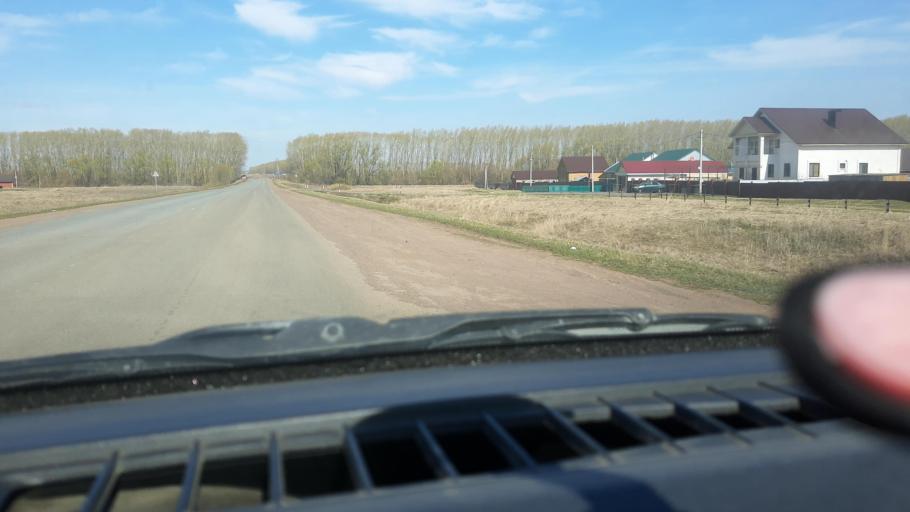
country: RU
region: Bashkortostan
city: Asanovo
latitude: 54.9676
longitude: 55.5422
